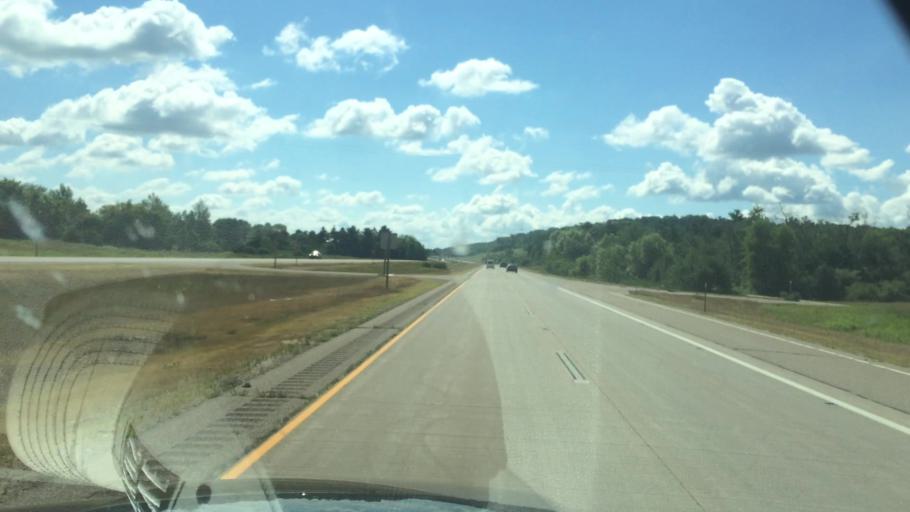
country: US
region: Wisconsin
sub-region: Waupaca County
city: King
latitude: 44.3809
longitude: -89.1746
